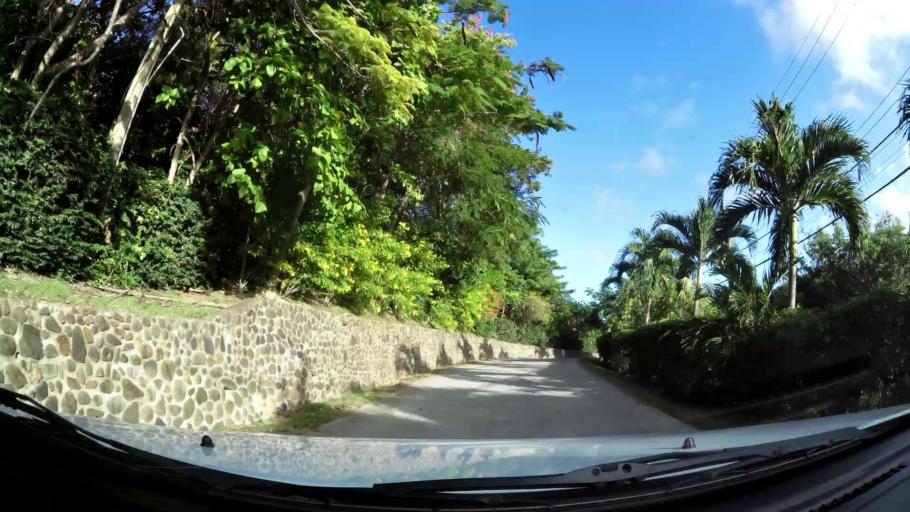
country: LC
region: Gros-Islet
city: Gros Islet
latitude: 14.1041
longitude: -60.9372
